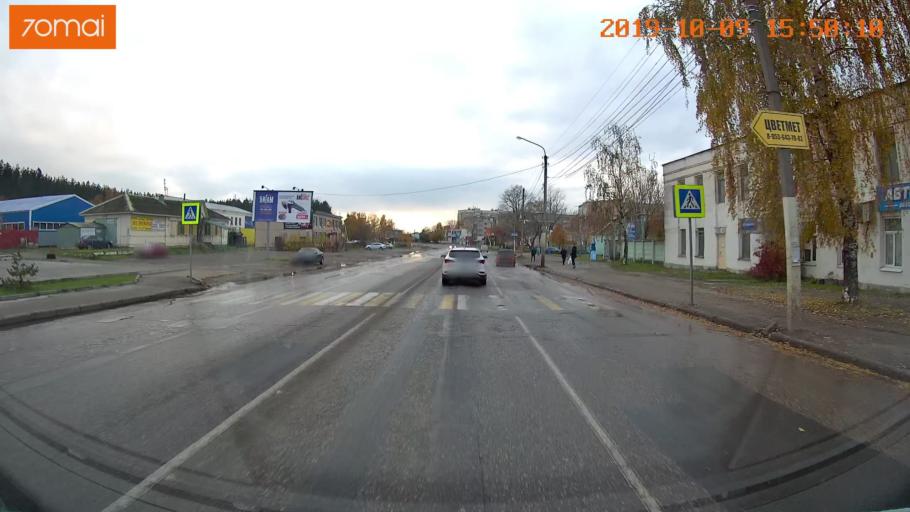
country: RU
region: Kostroma
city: Oktyabr'skiy
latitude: 57.8032
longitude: 40.9944
